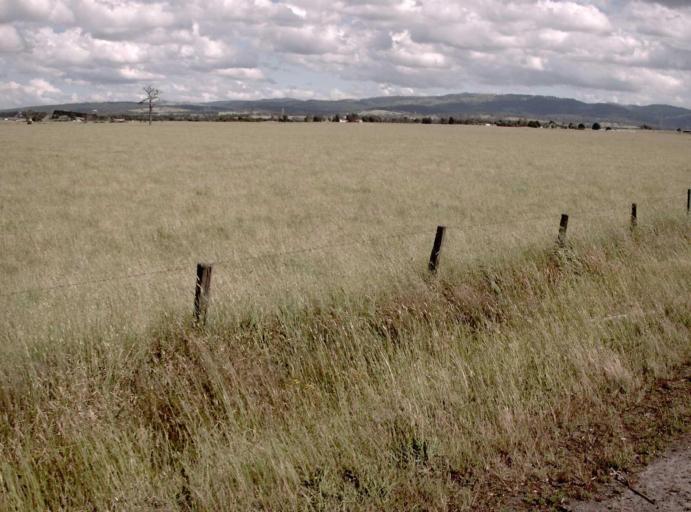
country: AU
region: Victoria
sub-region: Latrobe
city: Morwell
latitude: -38.2518
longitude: 146.4354
